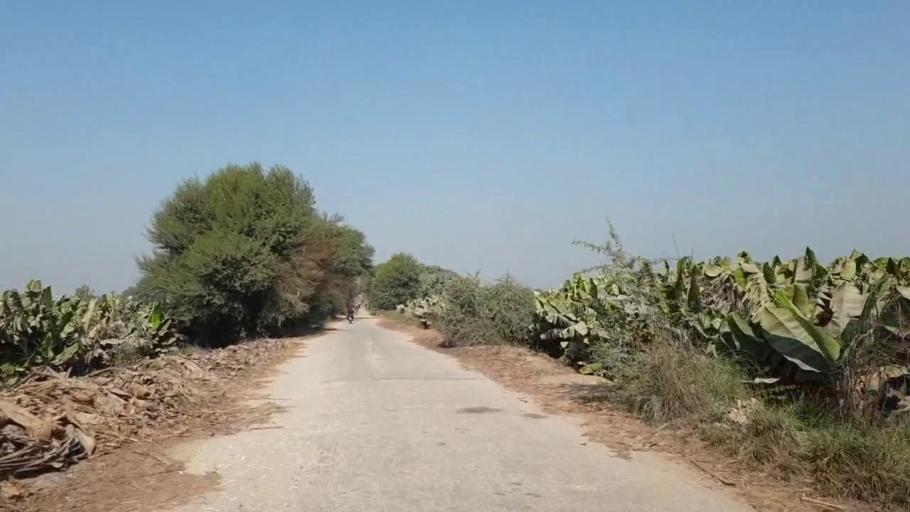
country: PK
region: Sindh
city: Matiari
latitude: 25.6042
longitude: 68.5986
